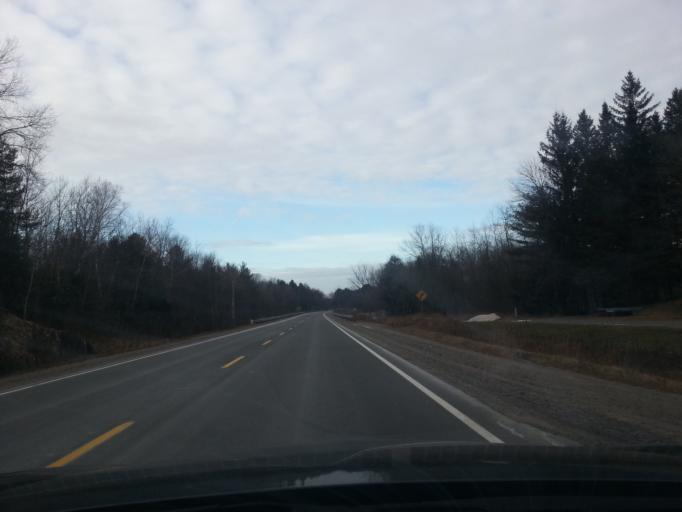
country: CA
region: Ontario
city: Belleville
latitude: 44.5408
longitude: -77.3590
